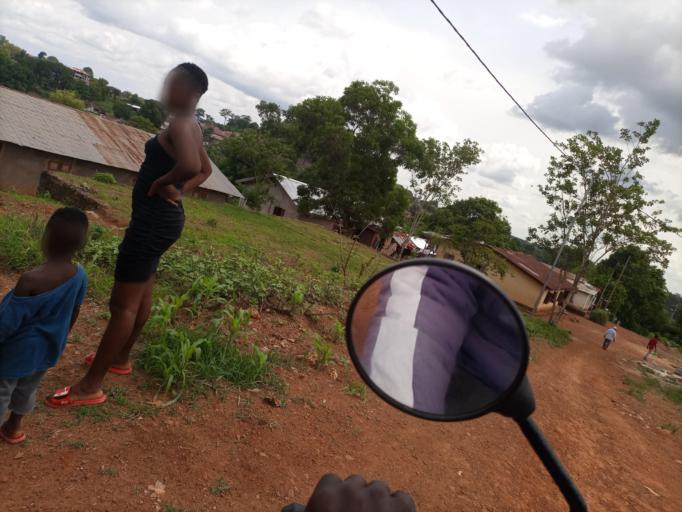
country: SL
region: Southern Province
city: Bo
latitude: 7.9503
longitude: -11.7404
